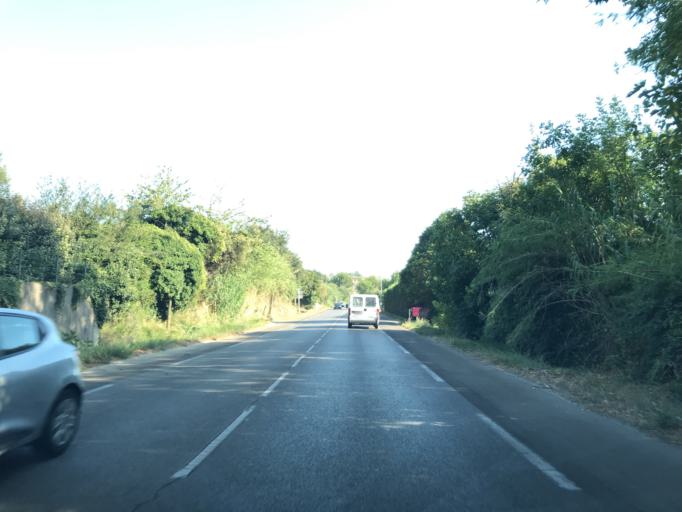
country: FR
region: Provence-Alpes-Cote d'Azur
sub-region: Departement des Bouches-du-Rhone
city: Saint-Chamas
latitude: 43.5610
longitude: 5.0302
